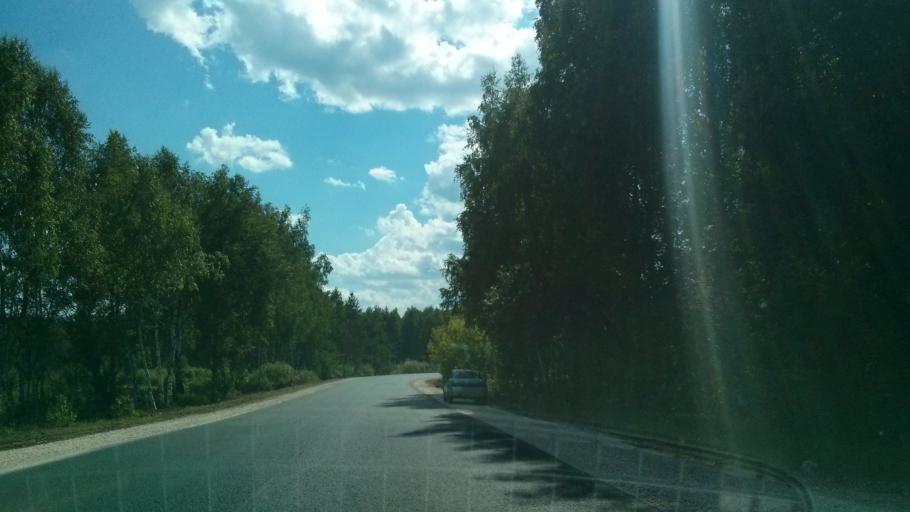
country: RU
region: Vladimir
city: Murom
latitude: 55.5001
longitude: 41.9076
